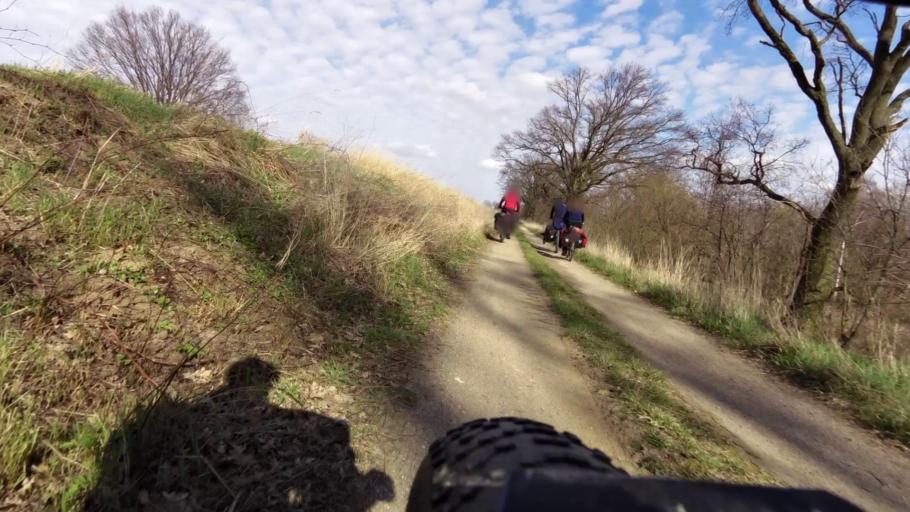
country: DE
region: Brandenburg
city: Reitwein
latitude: 52.4579
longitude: 14.6045
